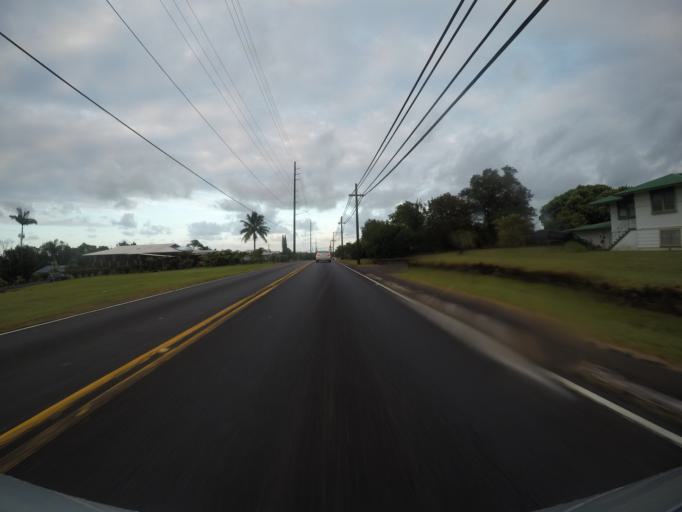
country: US
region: Hawaii
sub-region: Hawaii County
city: Hilo
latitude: 19.6843
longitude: -155.0734
